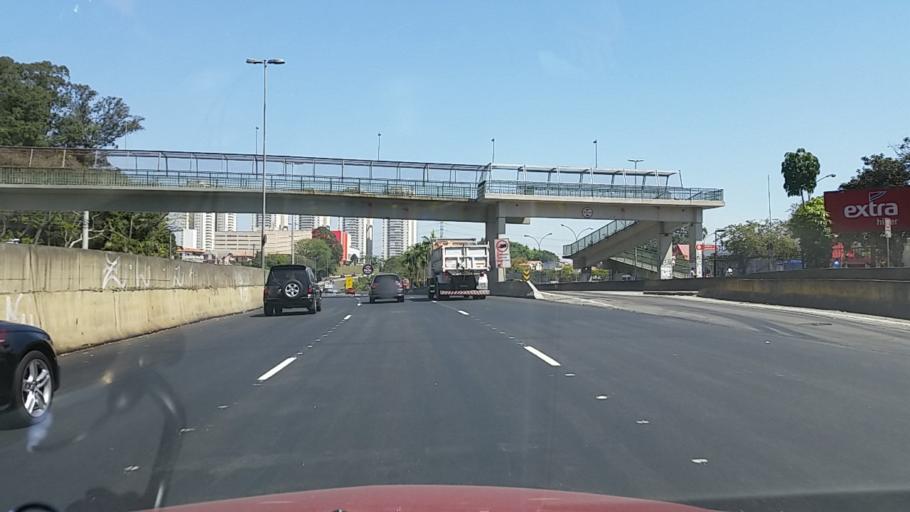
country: BR
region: Sao Paulo
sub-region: Taboao Da Serra
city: Taboao da Serra
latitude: -23.5853
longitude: -46.7464
